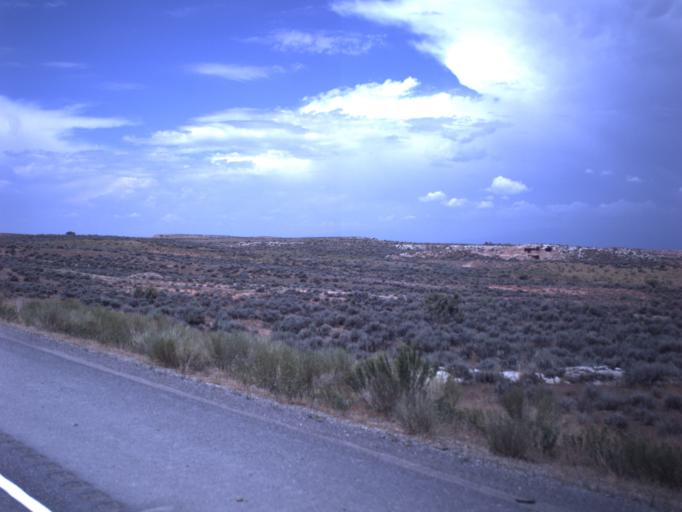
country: US
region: Utah
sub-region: Uintah County
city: Maeser
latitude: 40.3153
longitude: -109.7305
